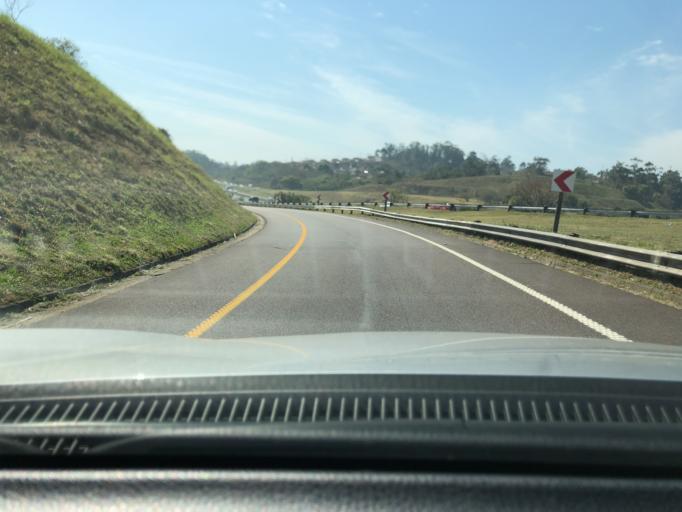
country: ZA
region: KwaZulu-Natal
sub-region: eThekwini Metropolitan Municipality
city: Berea
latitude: -29.8401
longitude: 30.9563
